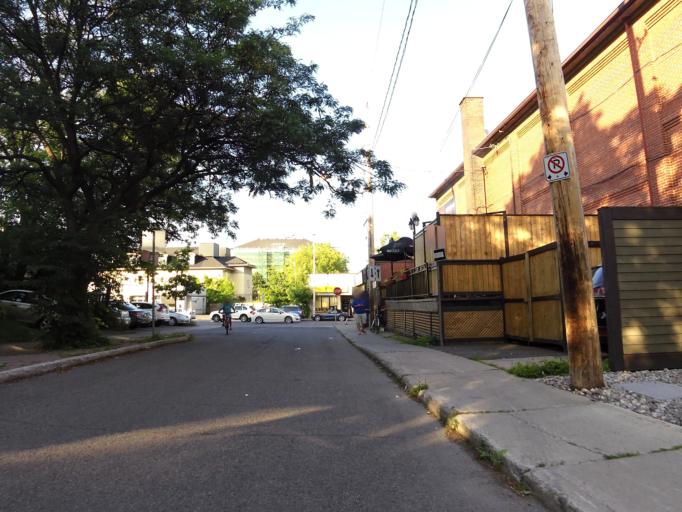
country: CA
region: Ontario
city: Ottawa
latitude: 45.3946
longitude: -75.6843
